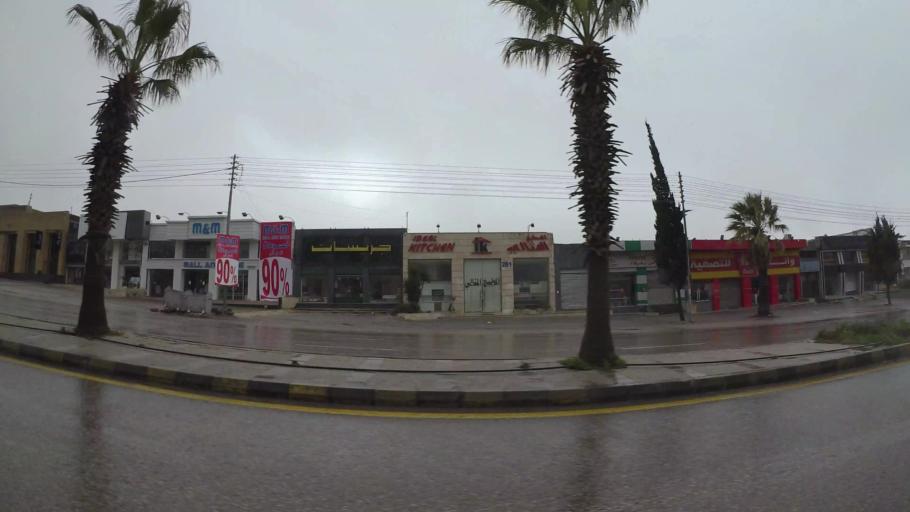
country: JO
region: Amman
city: Wadi as Sir
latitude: 31.9744
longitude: 35.8413
